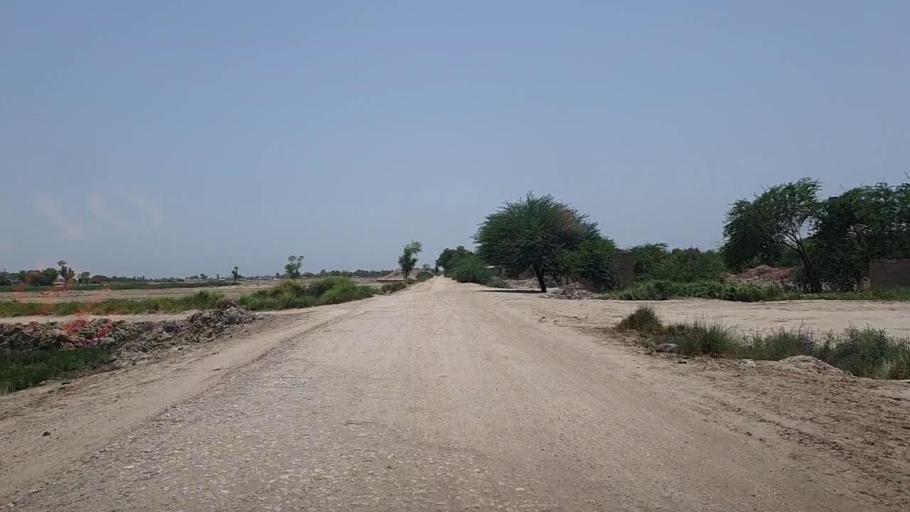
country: PK
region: Sindh
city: Pad Idan
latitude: 26.7678
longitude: 68.2936
